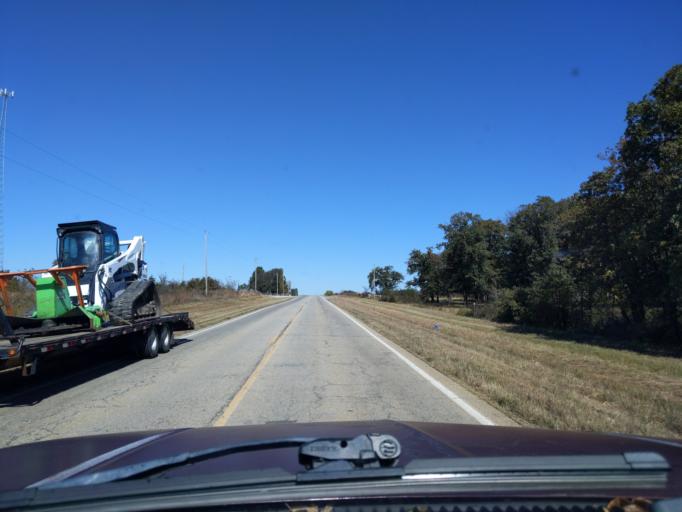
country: US
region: Oklahoma
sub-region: Creek County
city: Bristow
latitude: 35.7178
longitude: -96.3872
